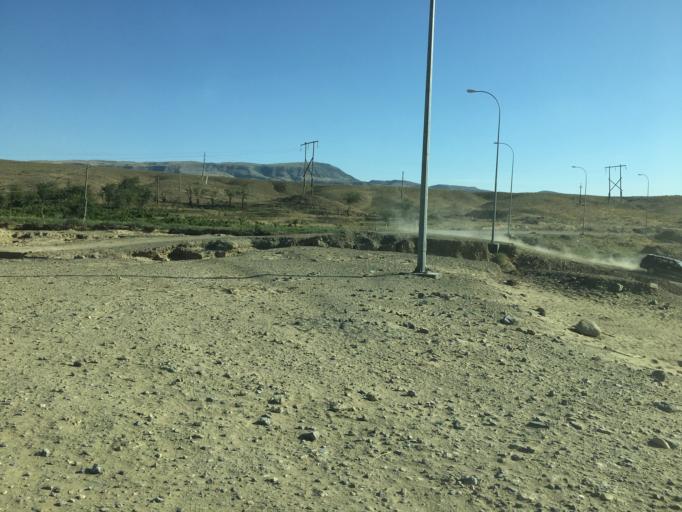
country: TM
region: Balkan
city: Magtymguly
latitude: 38.6308
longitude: 56.6203
